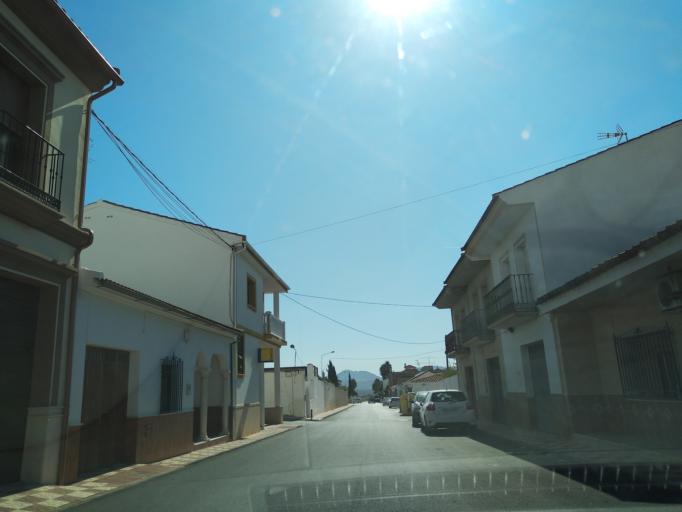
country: ES
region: Andalusia
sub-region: Provincia de Malaga
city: Mollina
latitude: 37.1236
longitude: -4.6563
